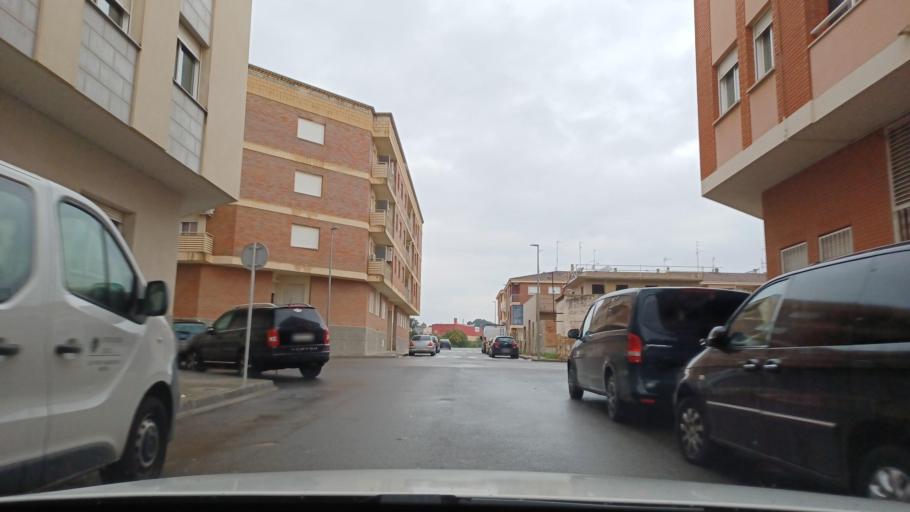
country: ES
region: Catalonia
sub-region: Provincia de Tarragona
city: Amposta
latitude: 40.7031
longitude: 0.5743
